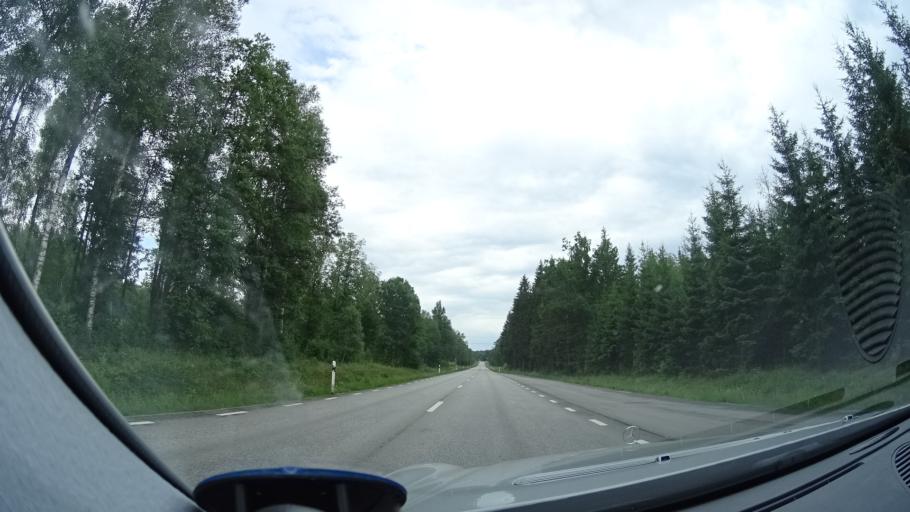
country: SE
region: Kronoberg
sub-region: Tingsryds Kommun
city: Tingsryd
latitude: 56.4790
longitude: 15.0042
